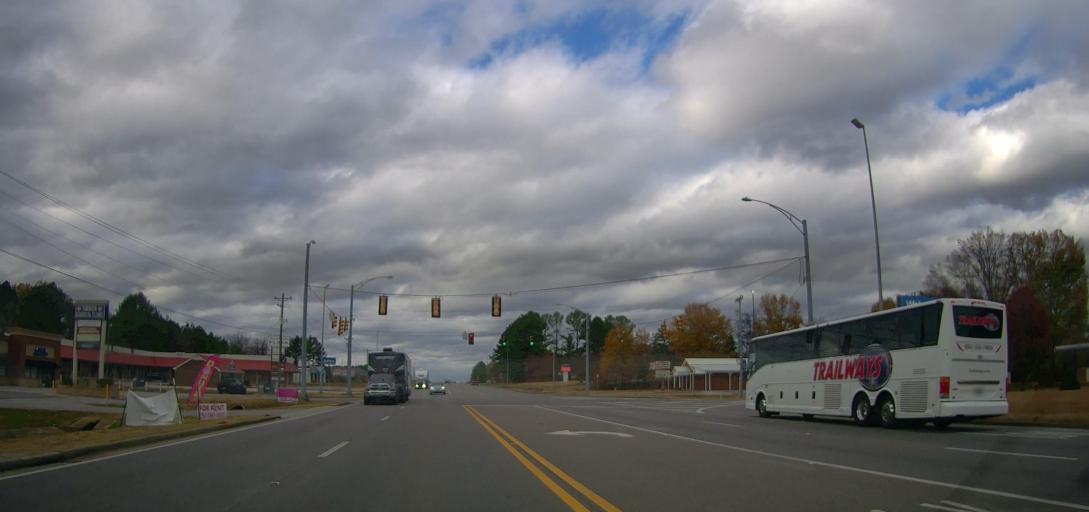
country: US
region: Alabama
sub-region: Lawrence County
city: Moulton
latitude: 34.4948
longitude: -87.2803
